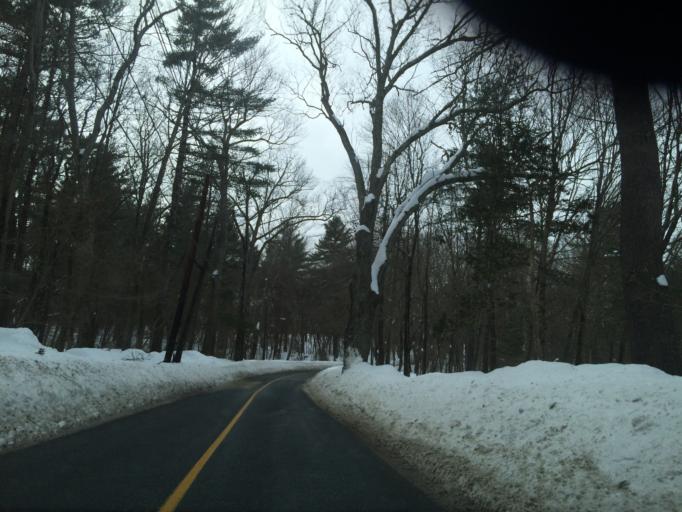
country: US
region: Massachusetts
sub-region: Middlesex County
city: Weston
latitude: 42.3830
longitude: -71.3090
